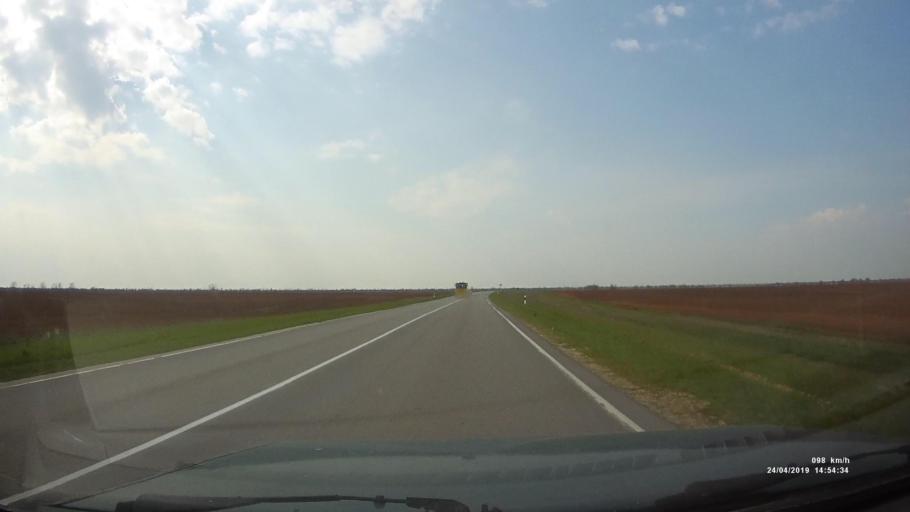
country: RU
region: Rostov
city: Remontnoye
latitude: 46.5353
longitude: 43.6366
